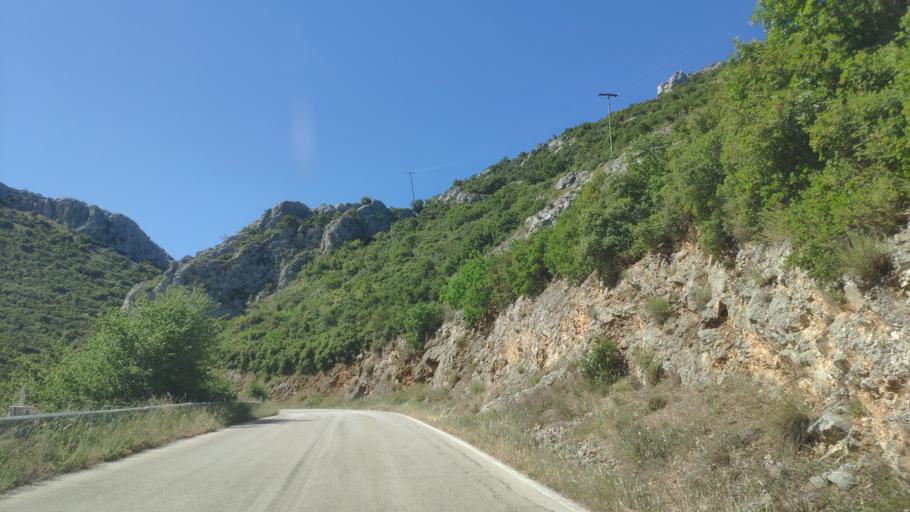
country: GR
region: Peloponnese
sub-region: Nomos Korinthias
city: Khiliomodhi
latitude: 37.7704
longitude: 22.8832
